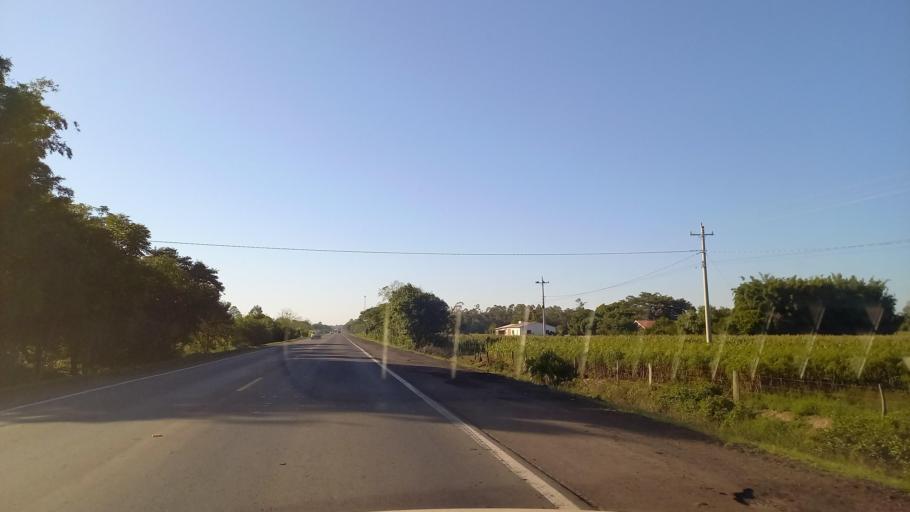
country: BR
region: Rio Grande do Sul
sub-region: Venancio Aires
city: Venancio Aires
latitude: -29.6623
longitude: -52.0645
